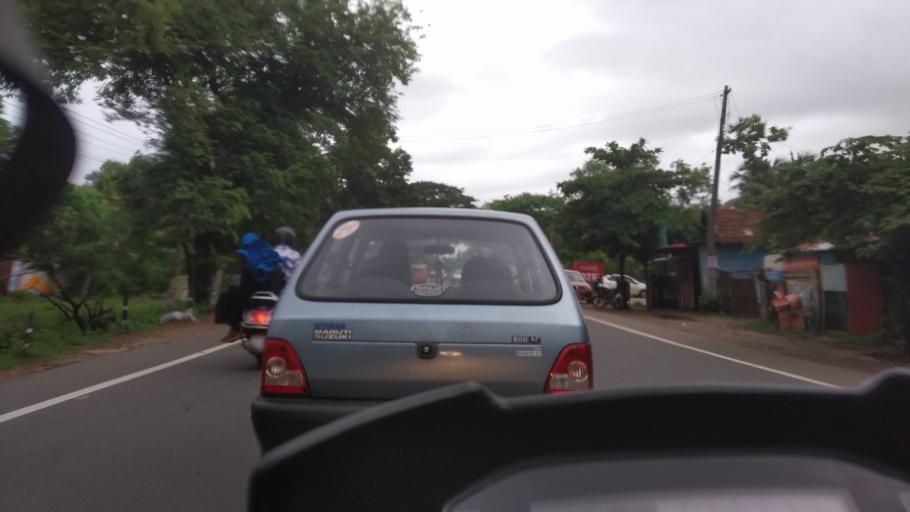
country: IN
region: Kerala
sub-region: Alappuzha
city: Alleppey
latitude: 9.4473
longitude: 76.3424
